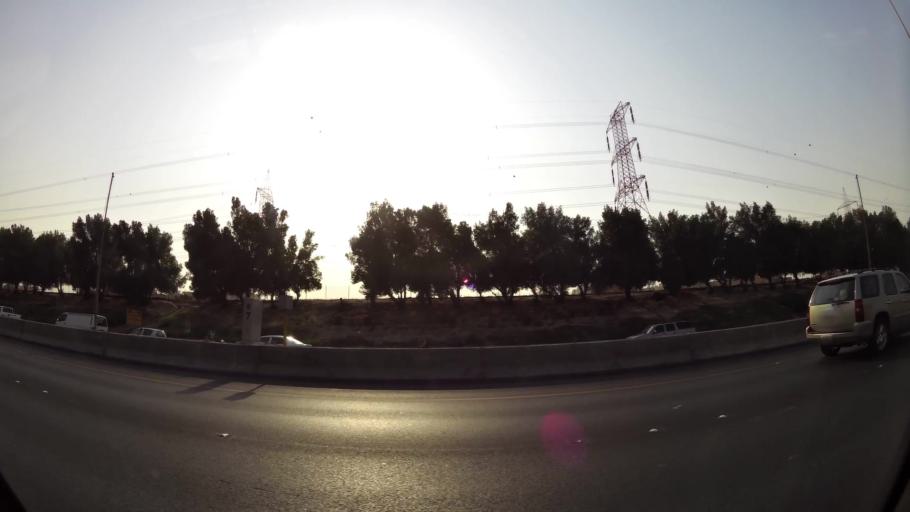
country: KW
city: Bayan
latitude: 29.3003
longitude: 48.0252
